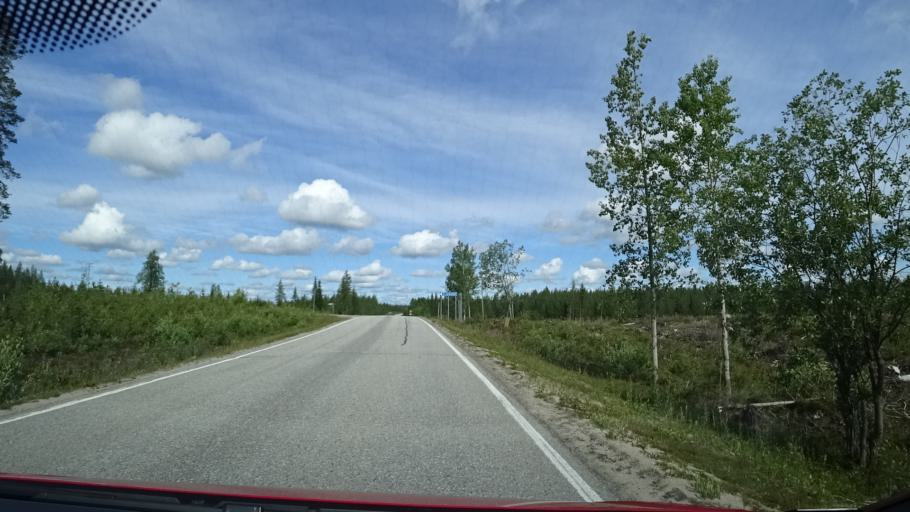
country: FI
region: Kainuu
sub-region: Kehys-Kainuu
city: Kuhmo
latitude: 64.4864
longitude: 29.7281
